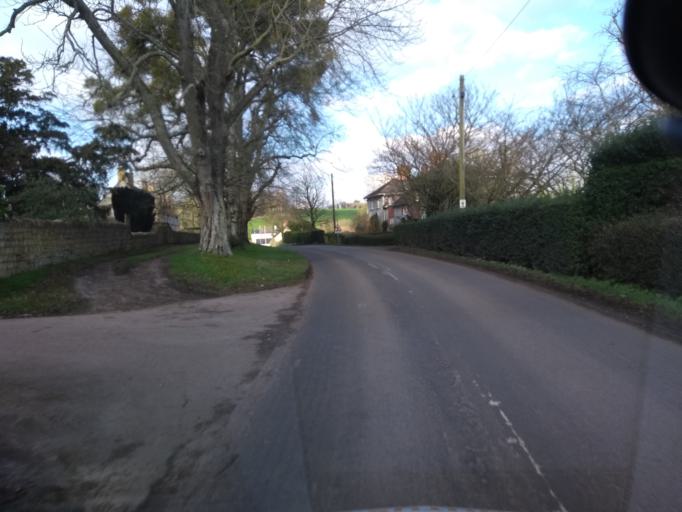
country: GB
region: England
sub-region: Somerset
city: Creech Saint Michael
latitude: 50.9587
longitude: -3.0486
